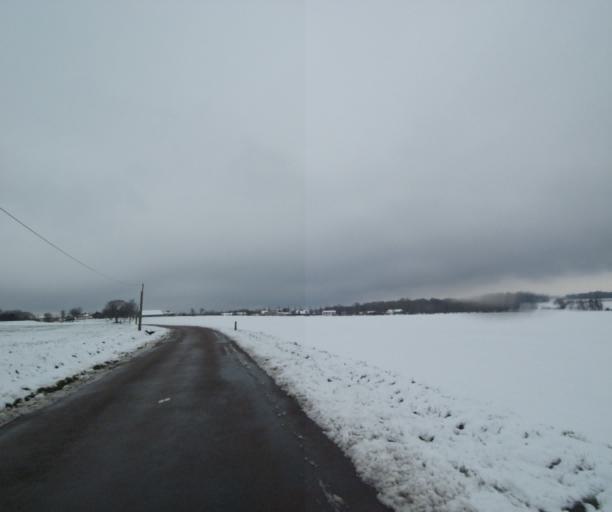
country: FR
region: Champagne-Ardenne
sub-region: Departement de la Haute-Marne
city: Laneuville-a-Remy
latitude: 48.5072
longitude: 4.8507
